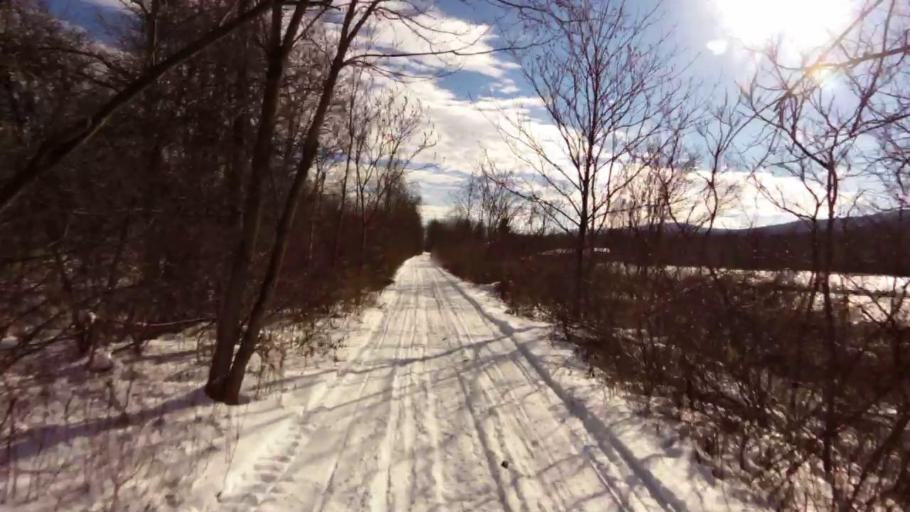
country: US
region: Pennsylvania
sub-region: McKean County
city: Foster Brook
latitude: 42.0524
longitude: -78.6365
